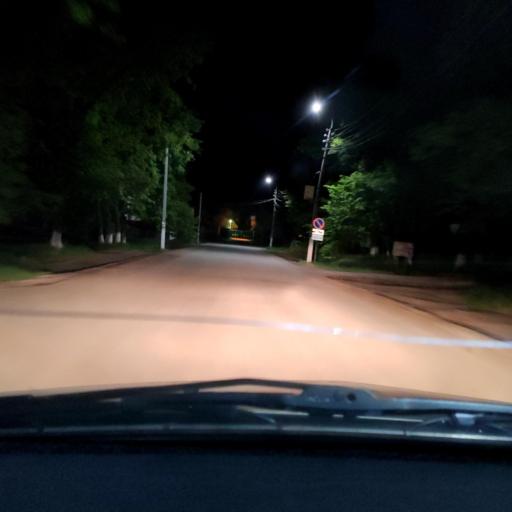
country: RU
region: Bashkortostan
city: Avdon
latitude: 54.6573
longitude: 55.5972
